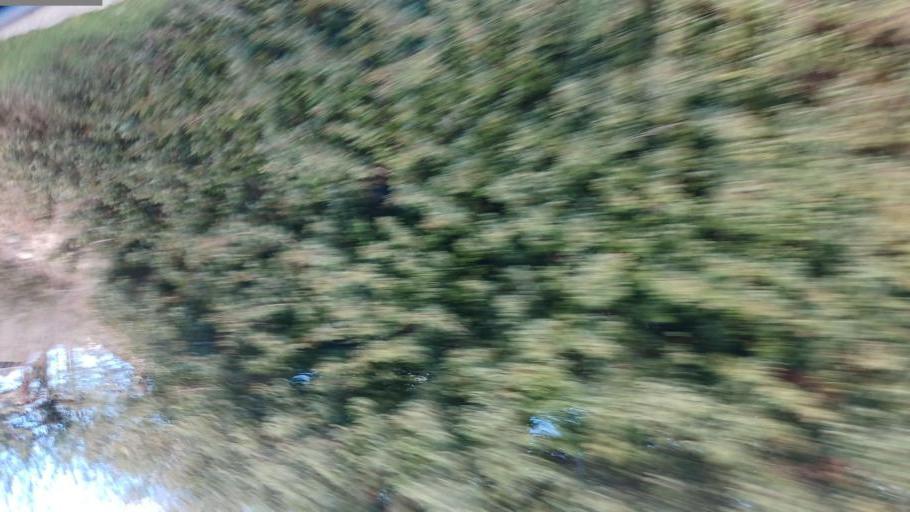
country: CY
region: Limassol
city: Pano Polemidia
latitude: 34.7607
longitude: 32.9831
